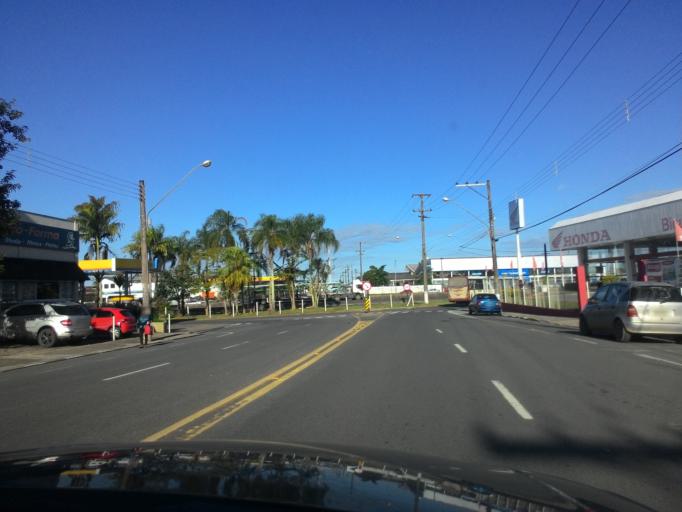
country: BR
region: Sao Paulo
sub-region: Registro
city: Registro
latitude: -24.5004
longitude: -47.8471
